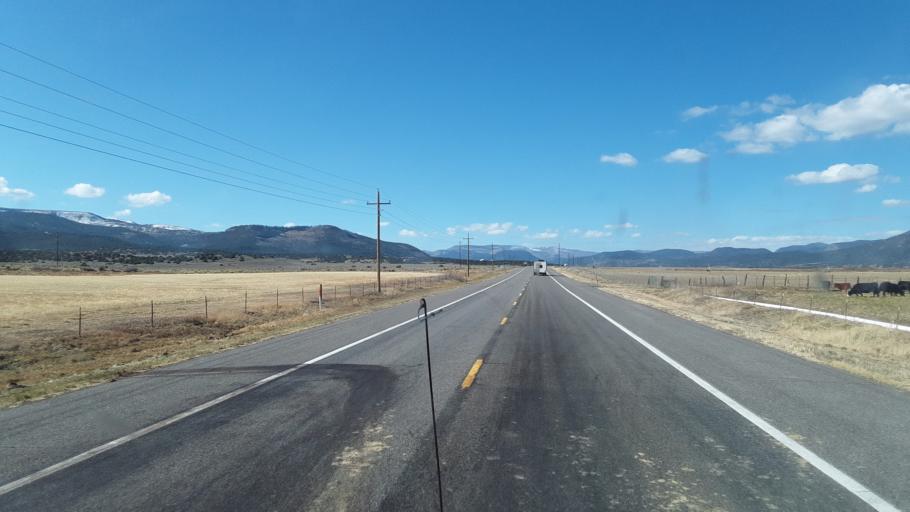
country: US
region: Colorado
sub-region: Rio Grande County
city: Del Norte
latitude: 37.6771
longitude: -106.4864
